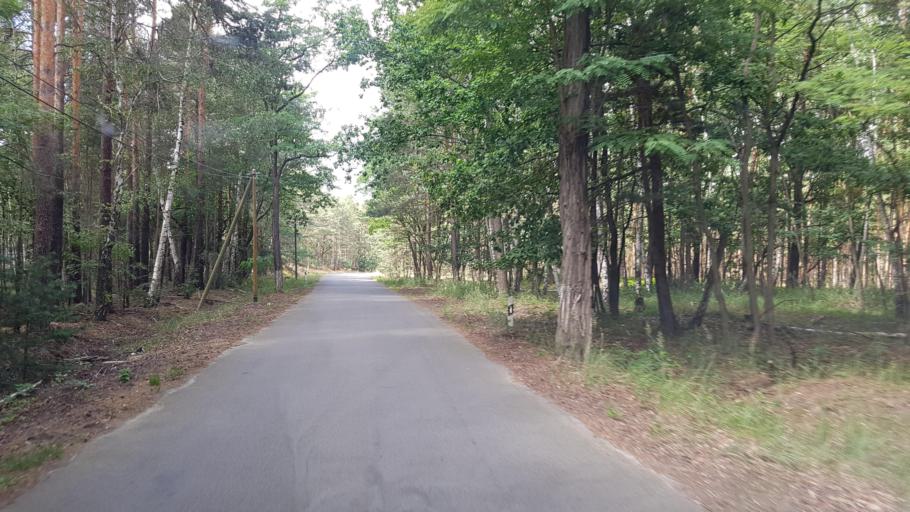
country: DE
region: Brandenburg
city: Altdobern
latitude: 51.6341
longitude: 14.0916
